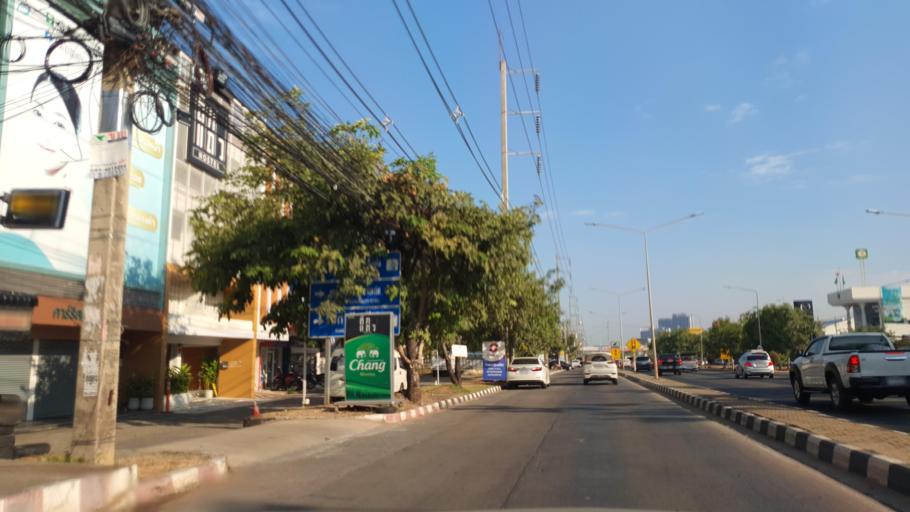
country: TH
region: Khon Kaen
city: Khon Kaen
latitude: 16.4184
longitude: 102.8195
